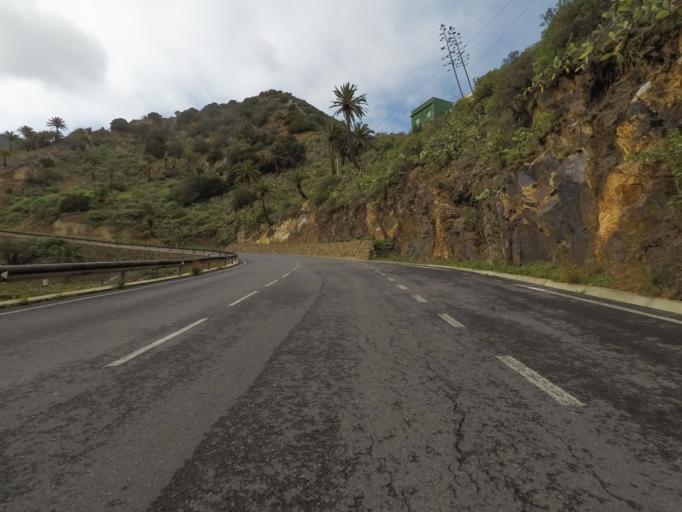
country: ES
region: Canary Islands
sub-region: Provincia de Santa Cruz de Tenerife
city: Vallehermosa
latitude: 28.1719
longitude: -17.2780
